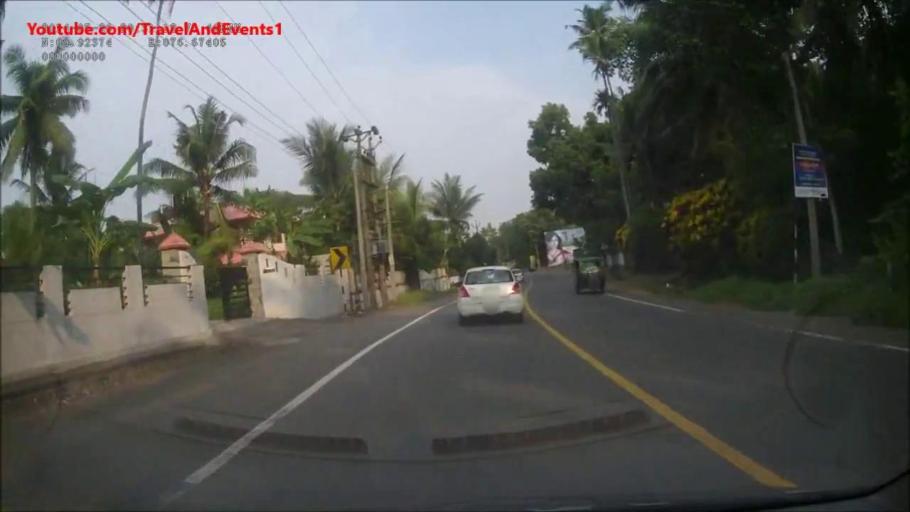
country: IN
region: Kerala
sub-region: Ernakulam
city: Muvattupula
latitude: 9.9234
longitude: 76.6744
